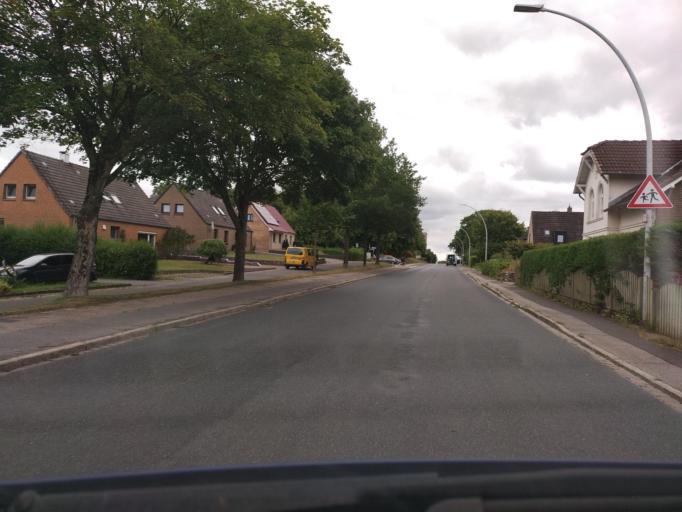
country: DE
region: Schleswig-Holstein
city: Schleswig
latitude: 54.5242
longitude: 9.5331
